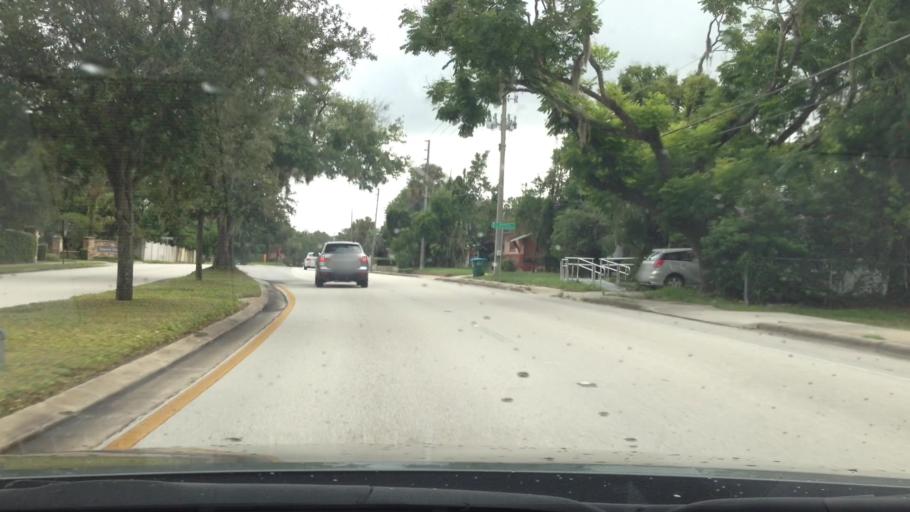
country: US
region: Florida
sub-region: Orange County
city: Maitland
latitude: 28.6272
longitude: -81.3521
